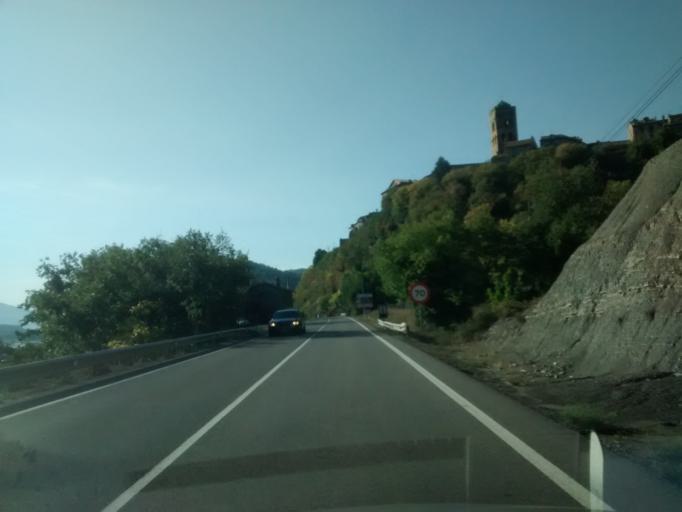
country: ES
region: Aragon
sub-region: Provincia de Huesca
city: Ainsa
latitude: 42.4193
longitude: 0.1399
